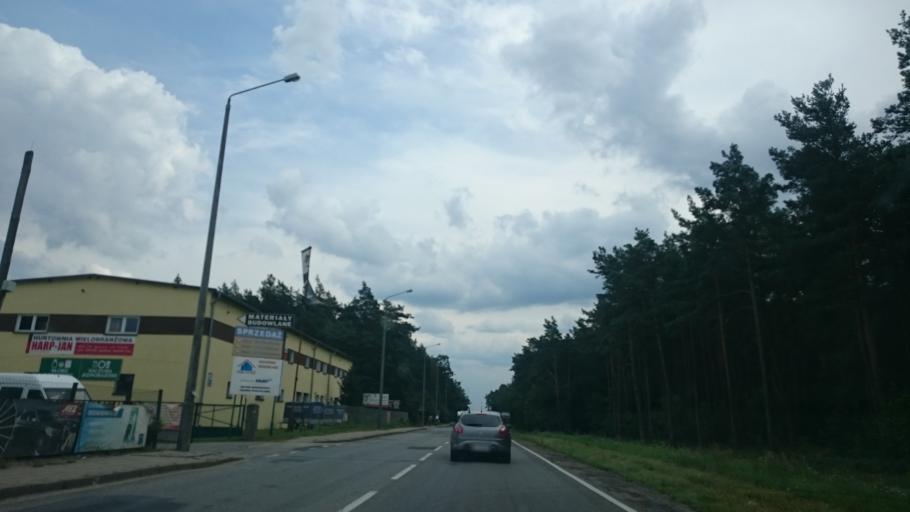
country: PL
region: Kujawsko-Pomorskie
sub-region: Powiat tucholski
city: Tuchola
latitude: 53.5772
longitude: 17.8793
